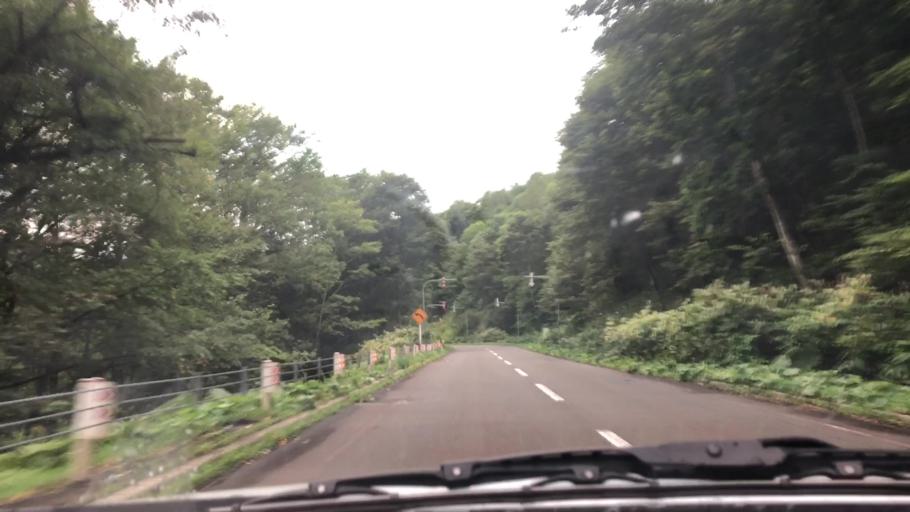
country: JP
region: Hokkaido
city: Shimo-furano
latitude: 42.9192
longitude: 142.3740
